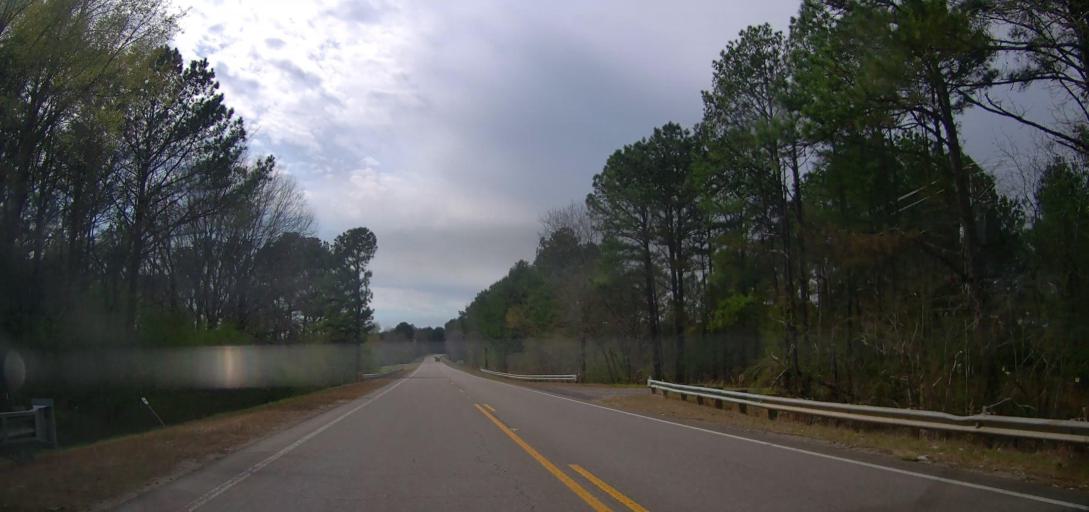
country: US
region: Alabama
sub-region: Walker County
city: Carbon Hill
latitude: 33.8765
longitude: -87.4804
